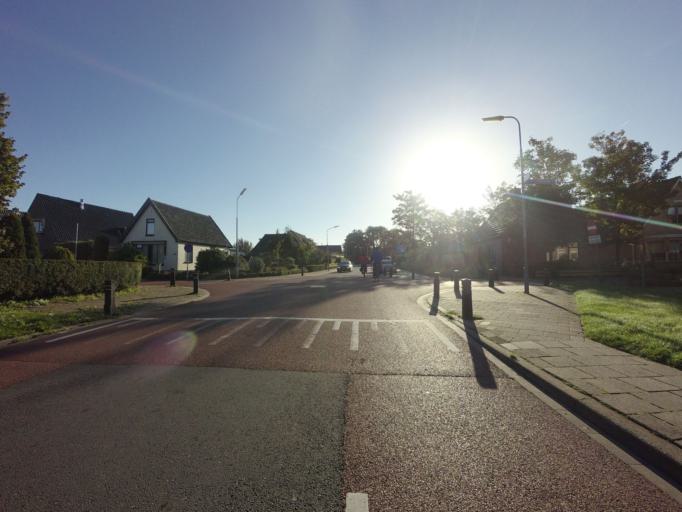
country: NL
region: North Holland
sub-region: Gemeente Langedijk
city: Broek op Langedijk
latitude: 52.6526
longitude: 4.7783
